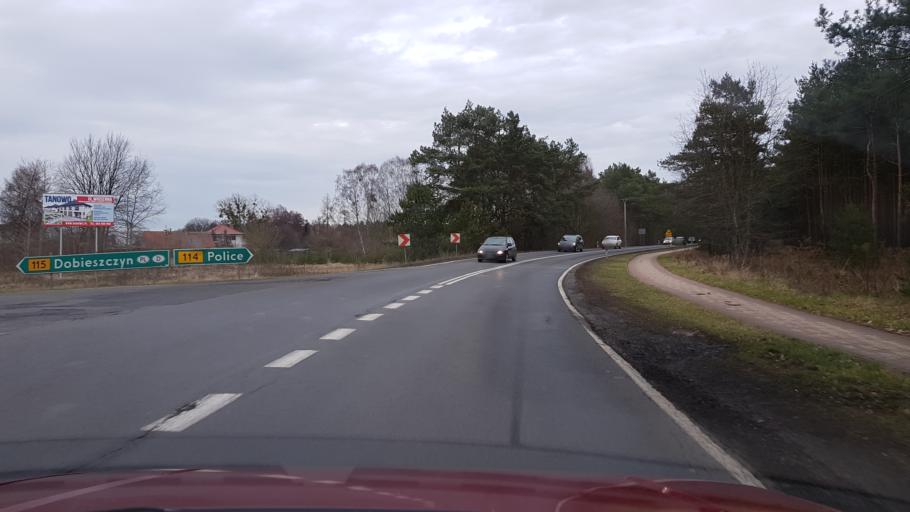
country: PL
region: West Pomeranian Voivodeship
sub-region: Powiat policki
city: Dobra
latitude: 53.5337
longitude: 14.4680
